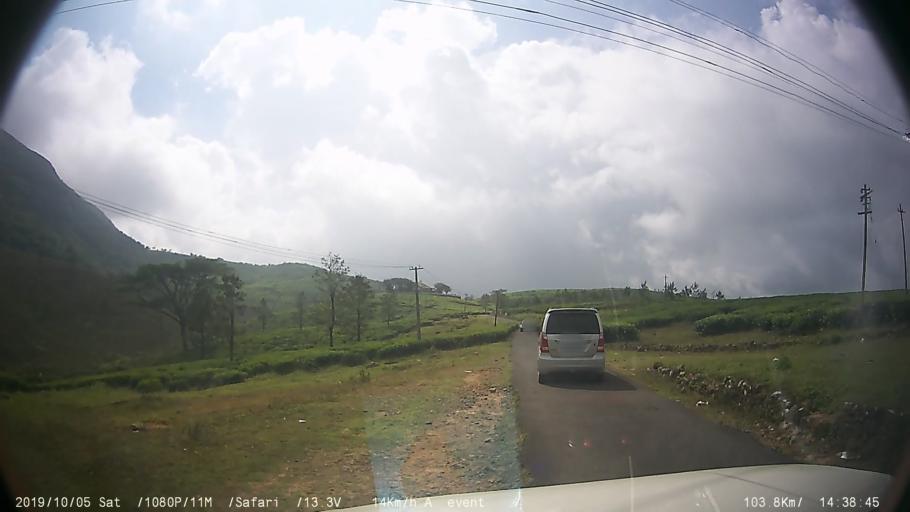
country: IN
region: Kerala
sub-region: Kottayam
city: Erattupetta
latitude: 9.6192
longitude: 76.9572
